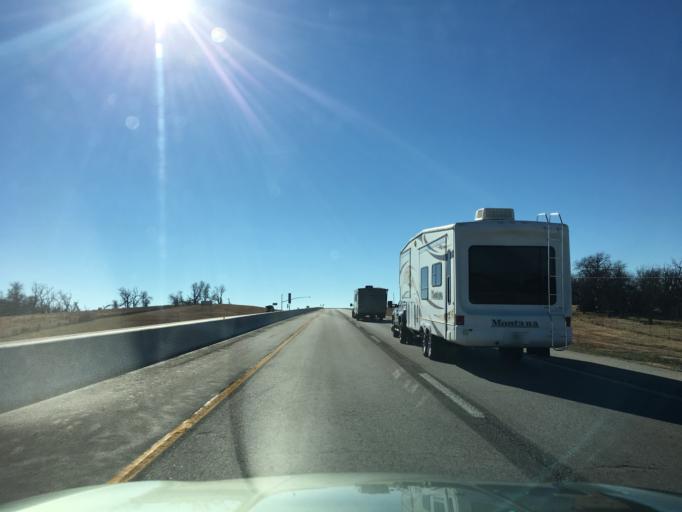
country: US
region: Oklahoma
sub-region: Kay County
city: Blackwell
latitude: 37.0055
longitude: -97.3407
